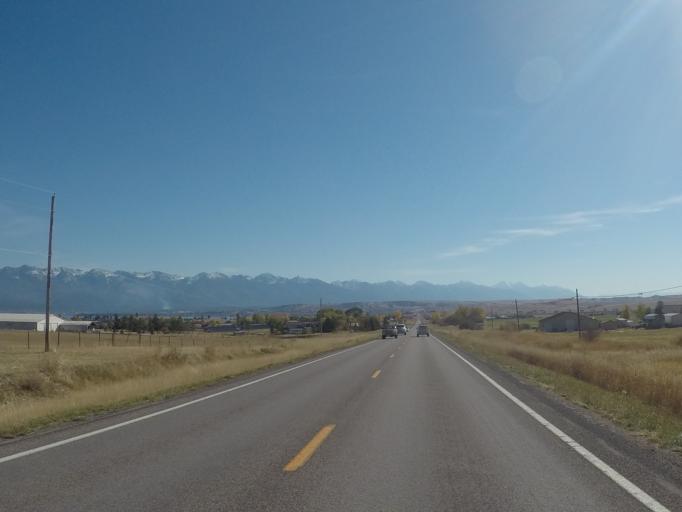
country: US
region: Montana
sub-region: Lake County
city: Polson
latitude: 47.7287
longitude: -114.2124
